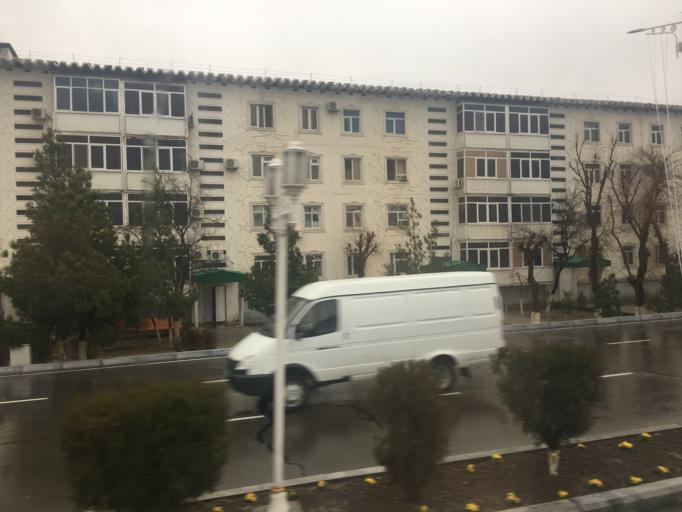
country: TM
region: Lebap
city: Turkmenabat
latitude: 39.0969
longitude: 63.5859
